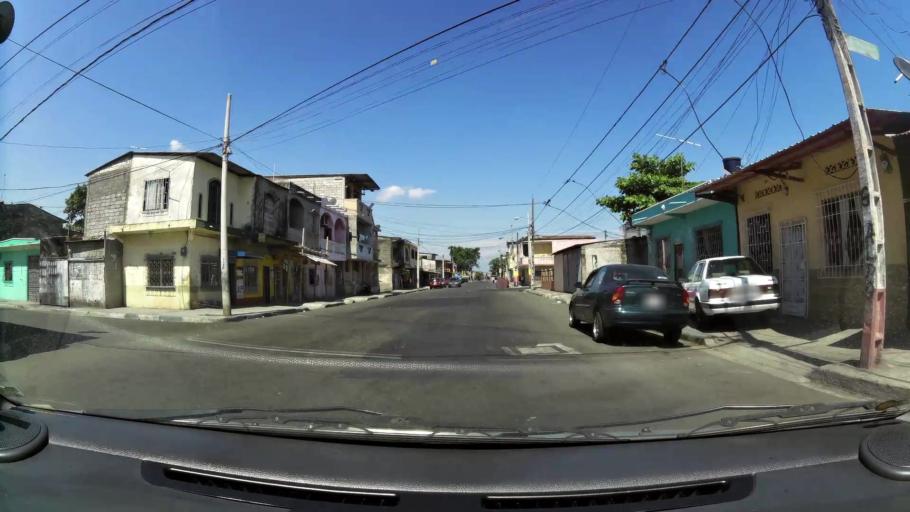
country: EC
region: Guayas
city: Guayaquil
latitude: -2.2246
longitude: -79.9347
